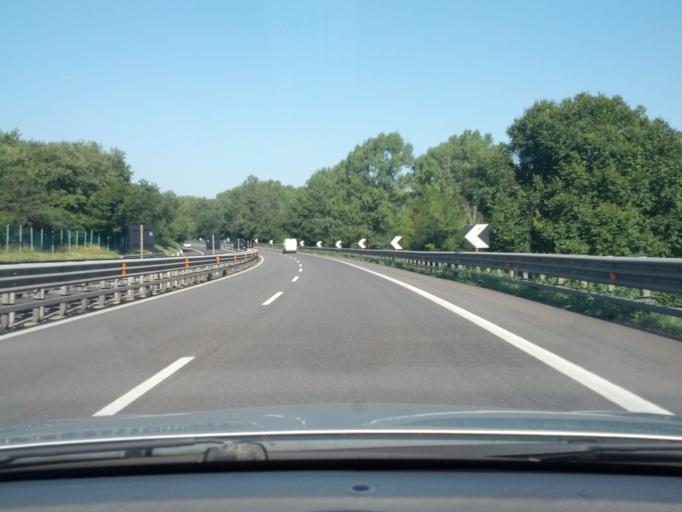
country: IT
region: Friuli Venezia Giulia
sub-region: Provincia di Gorizia
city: Monfalcone
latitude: 45.8156
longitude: 13.5569
